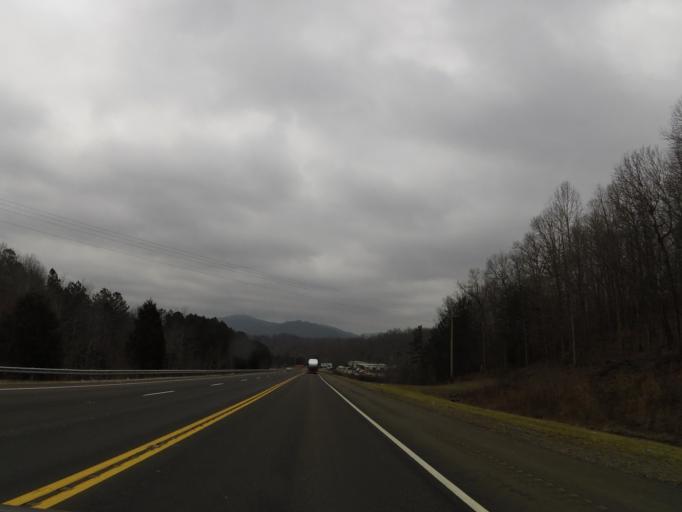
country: US
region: Tennessee
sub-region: Scott County
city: Huntsville
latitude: 36.3889
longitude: -84.4281
